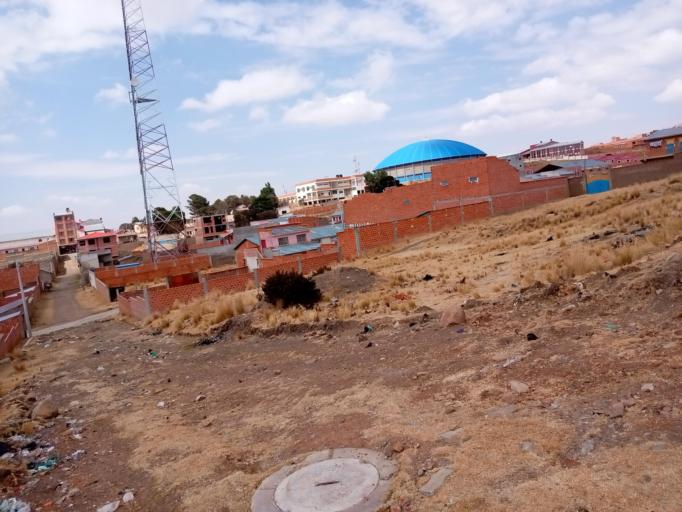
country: BO
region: La Paz
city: Batallas
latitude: -16.3983
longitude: -68.4796
